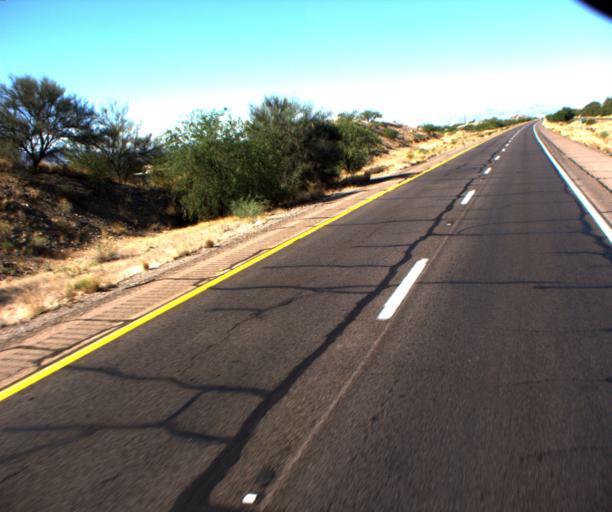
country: US
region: Arizona
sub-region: Pima County
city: Green Valley
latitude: 31.8219
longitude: -111.0051
